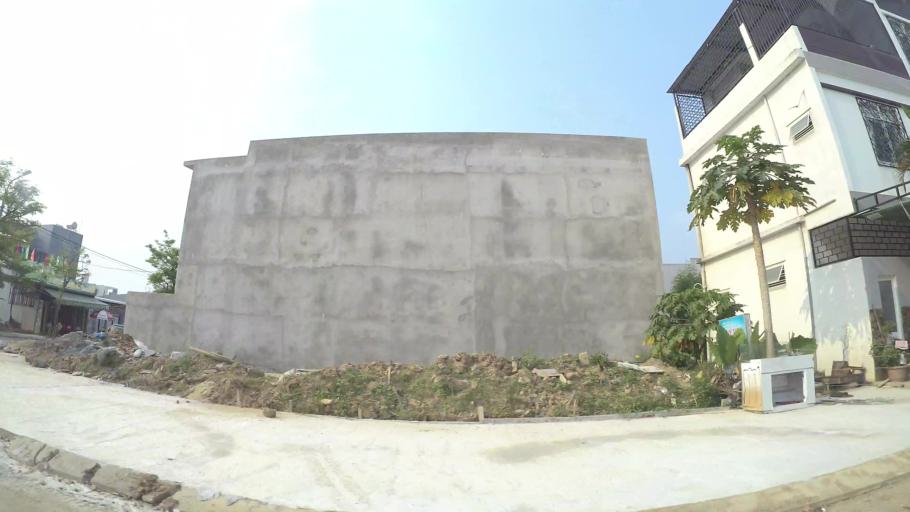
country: VN
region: Da Nang
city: Cam Le
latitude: 16.0085
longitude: 108.2266
